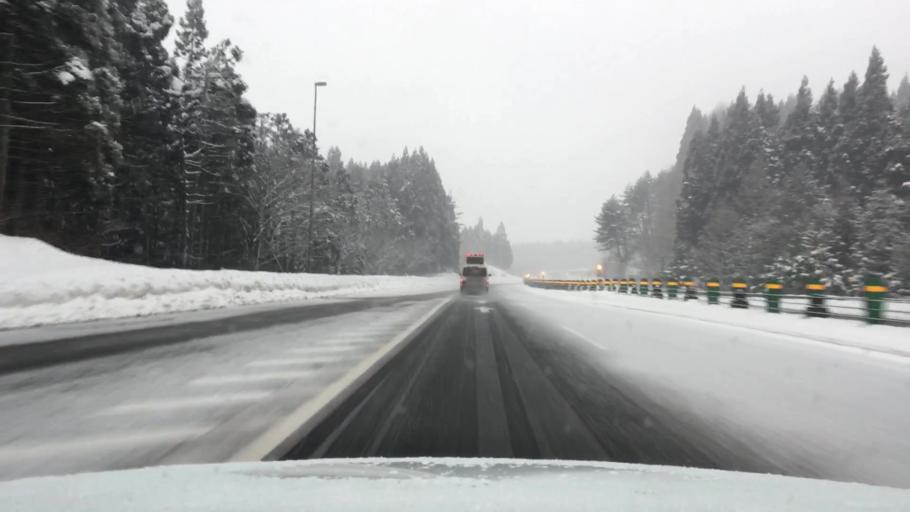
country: JP
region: Akita
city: Hanawa
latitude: 40.1650
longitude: 140.8021
